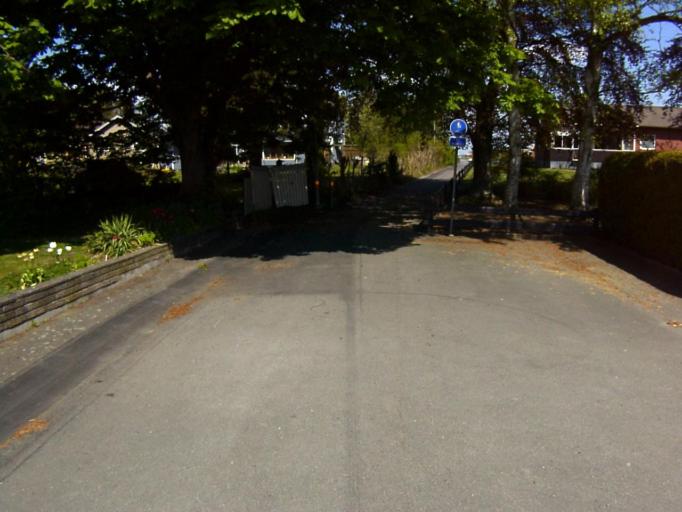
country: SE
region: Skane
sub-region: Kristianstads Kommun
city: Fjalkinge
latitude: 56.0152
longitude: 14.2270
